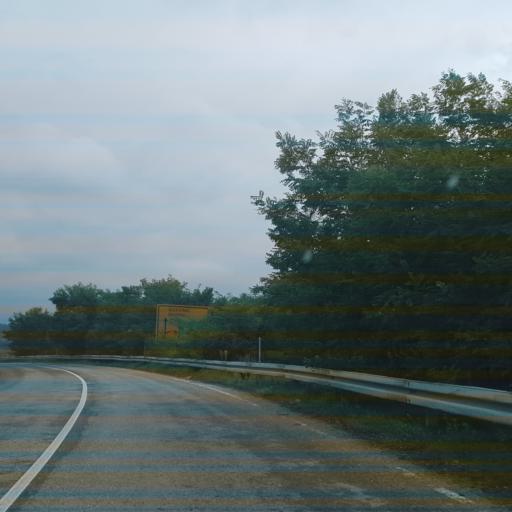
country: RS
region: Central Serbia
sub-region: Nisavski Okrug
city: Razanj
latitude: 43.6860
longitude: 21.5447
